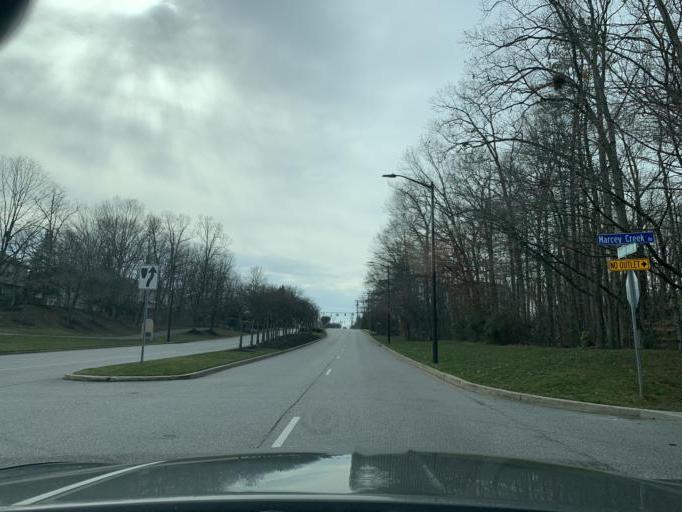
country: US
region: Maryland
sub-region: Anne Arundel County
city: Maryland City
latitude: 39.1013
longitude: -76.8098
